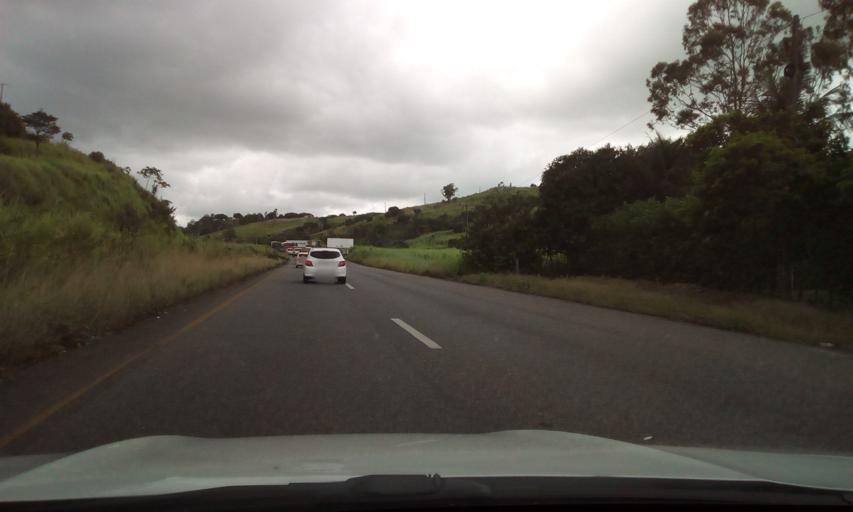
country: BR
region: Pernambuco
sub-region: Moreno
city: Moreno
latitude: -8.1107
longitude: -35.1522
